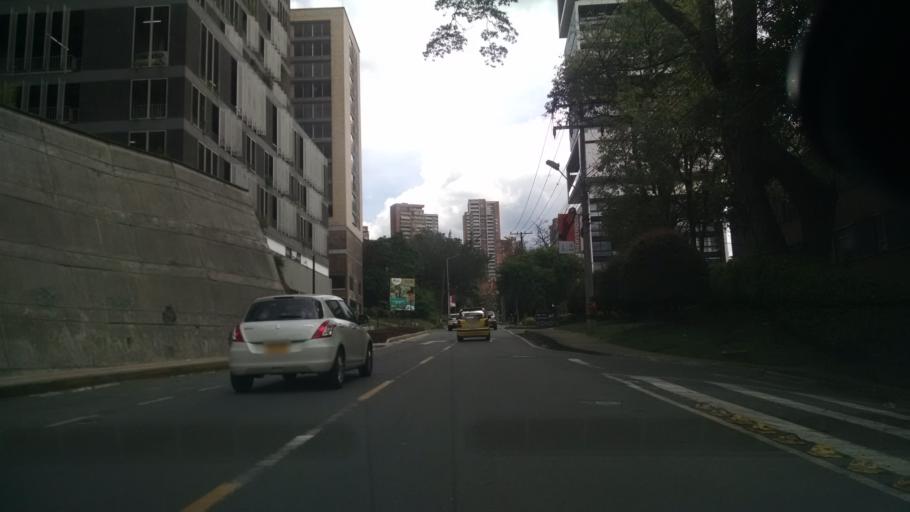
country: CO
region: Antioquia
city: Medellin
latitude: 6.2123
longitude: -75.5593
